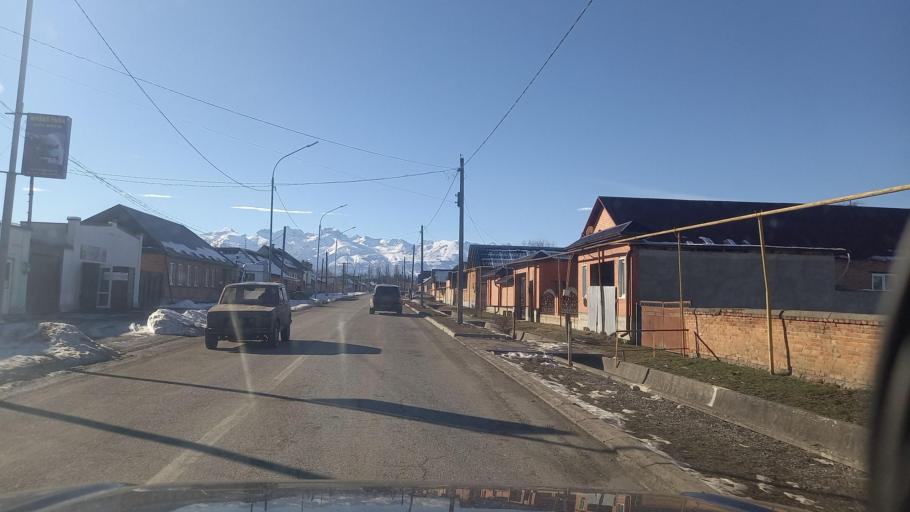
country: RU
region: North Ossetia
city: Chikola
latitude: 43.1898
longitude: 43.9072
